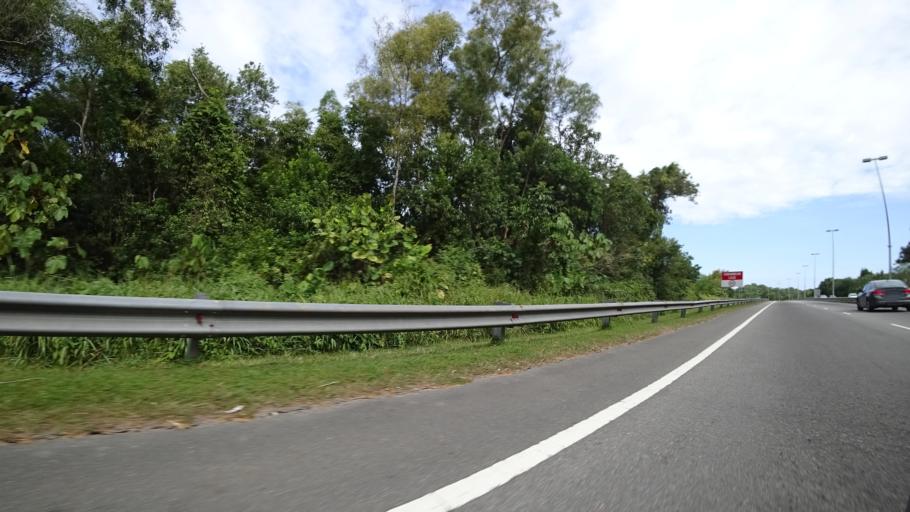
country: BN
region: Brunei and Muara
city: Bandar Seri Begawan
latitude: 4.9262
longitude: 114.9111
